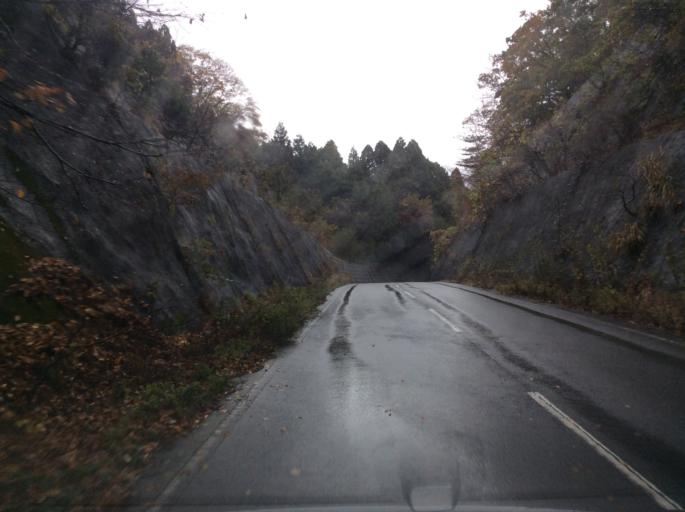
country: JP
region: Fukushima
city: Iwaki
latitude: 37.1063
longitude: 140.9311
